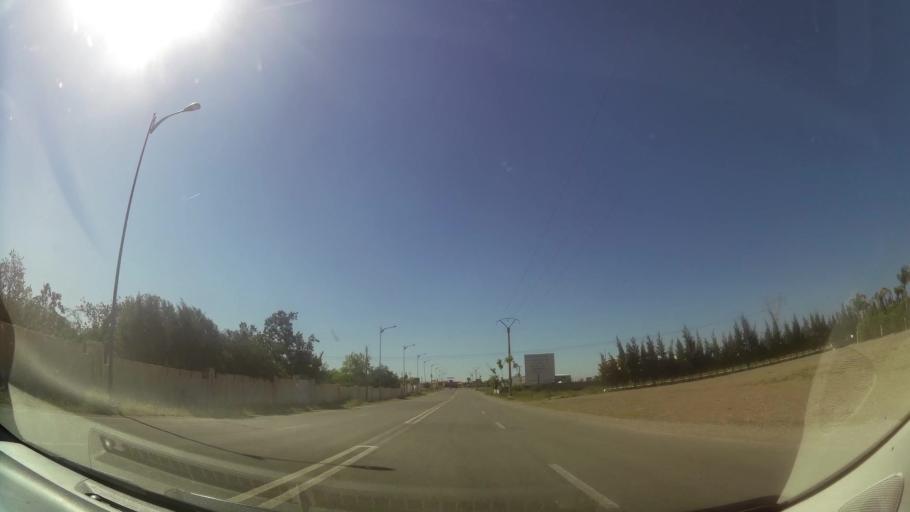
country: MA
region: Oriental
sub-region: Oujda-Angad
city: Oujda
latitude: 34.7296
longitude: -1.8704
